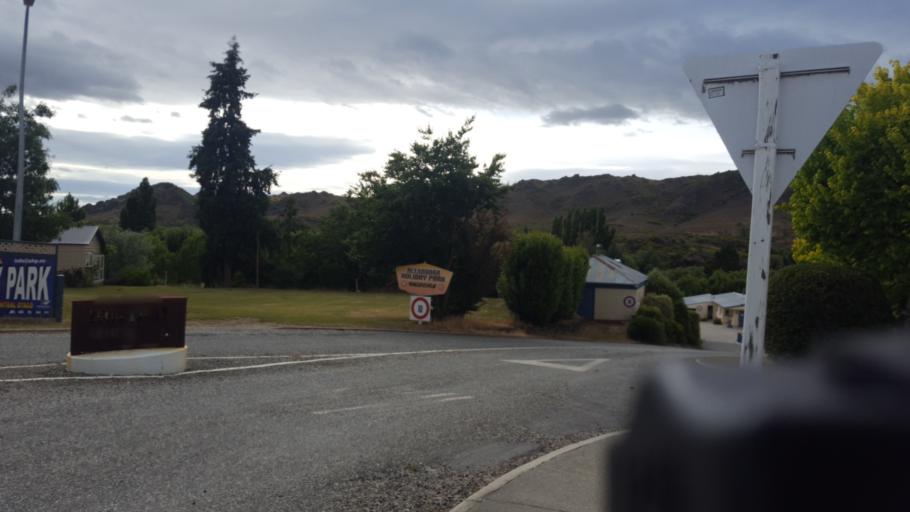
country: NZ
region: Otago
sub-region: Queenstown-Lakes District
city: Wanaka
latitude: -45.2450
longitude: 169.4035
